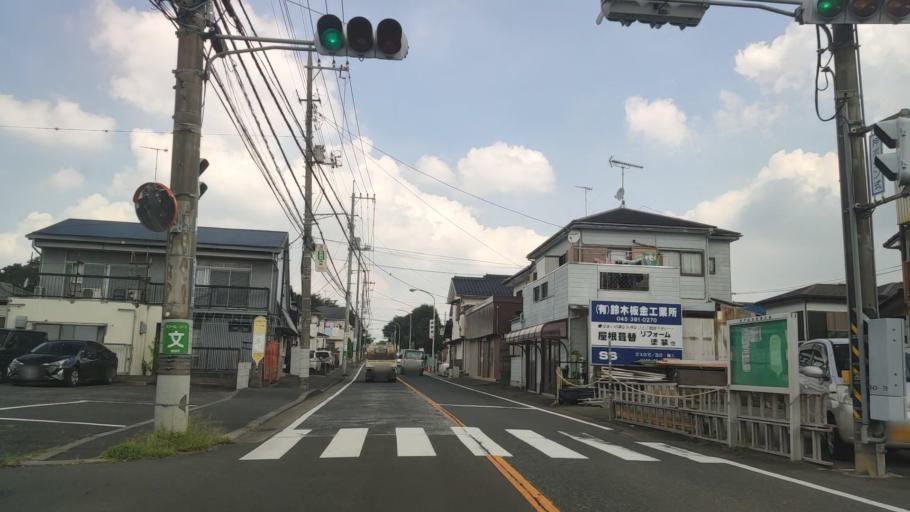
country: JP
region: Kanagawa
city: Minami-rinkan
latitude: 35.4529
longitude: 139.5025
